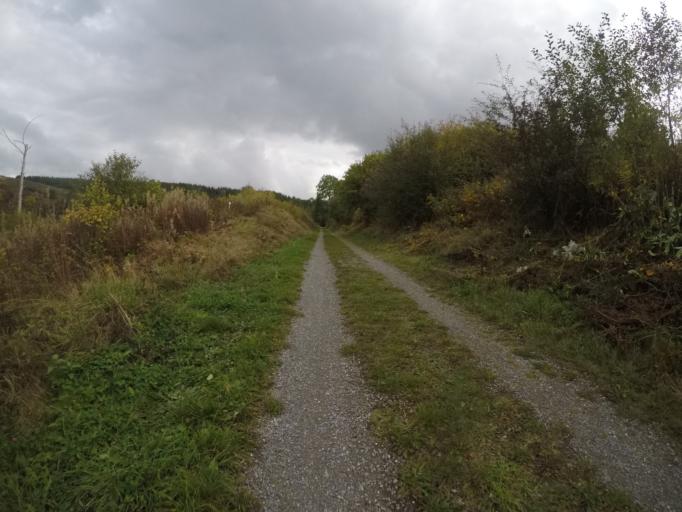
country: BE
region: Wallonia
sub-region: Province du Luxembourg
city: Fauvillers
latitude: 49.8873
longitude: 5.6754
